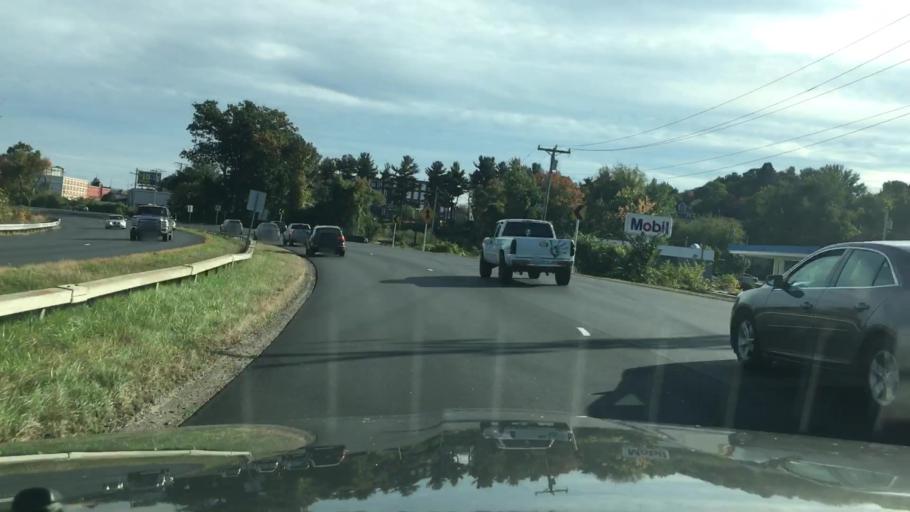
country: US
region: New Hampshire
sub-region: Hillsborough County
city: Manchester
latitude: 42.9995
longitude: -71.4750
